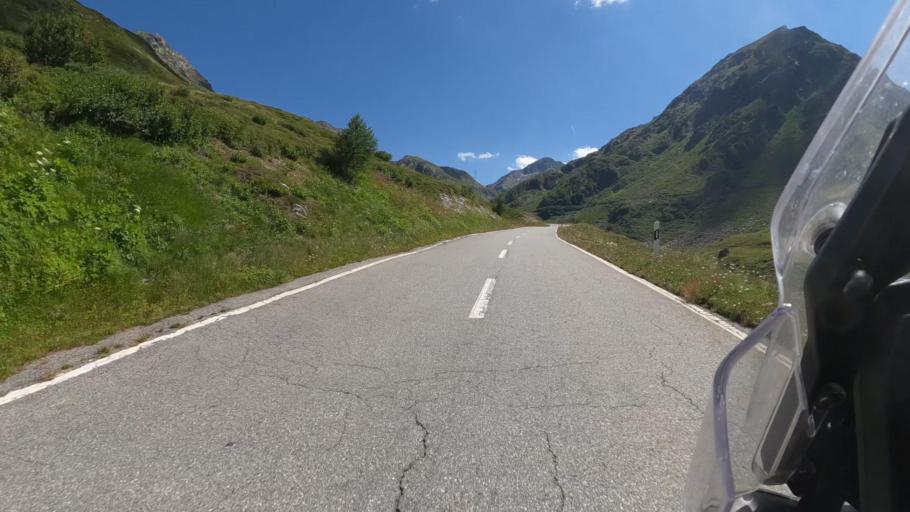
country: IT
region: Aosta Valley
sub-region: Valle d'Aosta
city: San Leonardo
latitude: 45.8960
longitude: 7.1869
